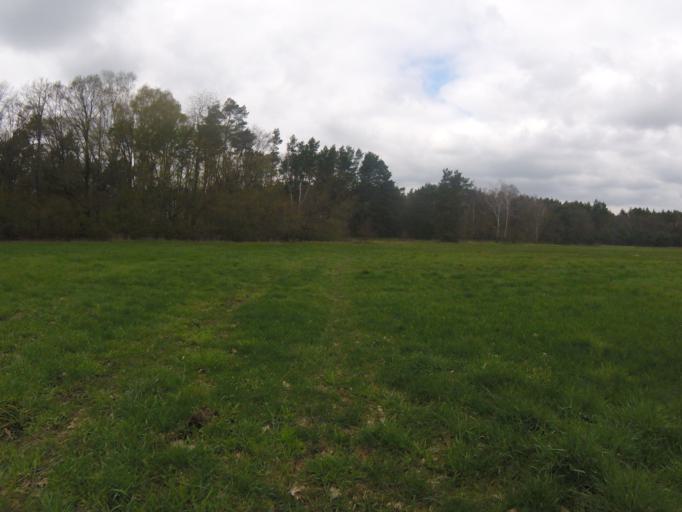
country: DE
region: Brandenburg
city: Mittenwalde
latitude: 52.2640
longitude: 13.5904
